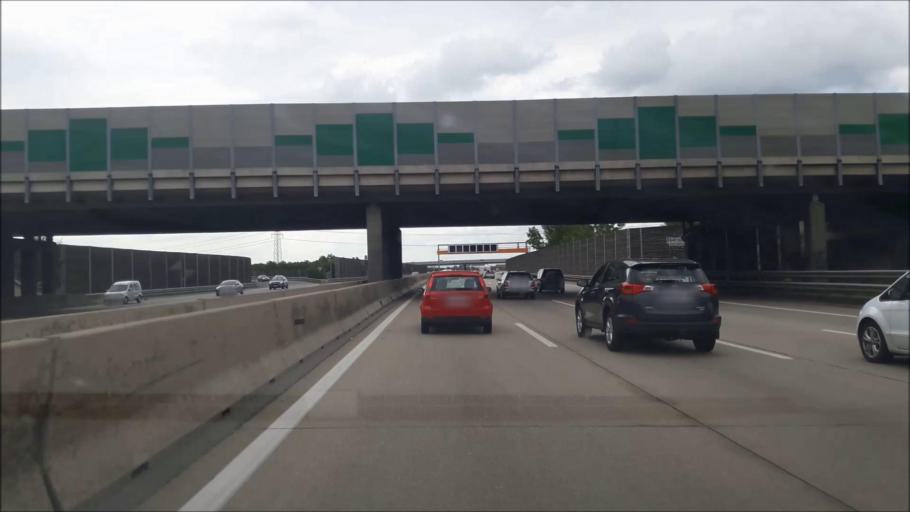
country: AT
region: Lower Austria
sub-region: Politischer Bezirk Modling
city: Biedermannsdorf
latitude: 48.0816
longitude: 16.3343
